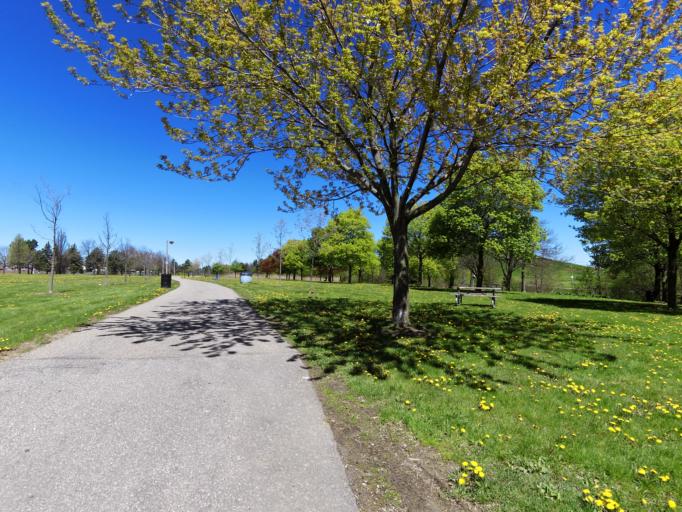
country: CA
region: Ontario
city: Brampton
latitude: 43.7249
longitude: -79.7259
